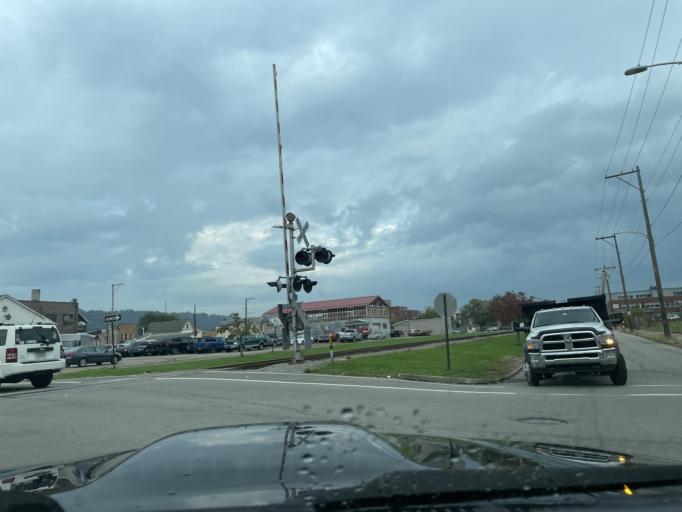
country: US
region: Pennsylvania
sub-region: Westmoreland County
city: New Kensington
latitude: 40.5627
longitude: -79.7631
